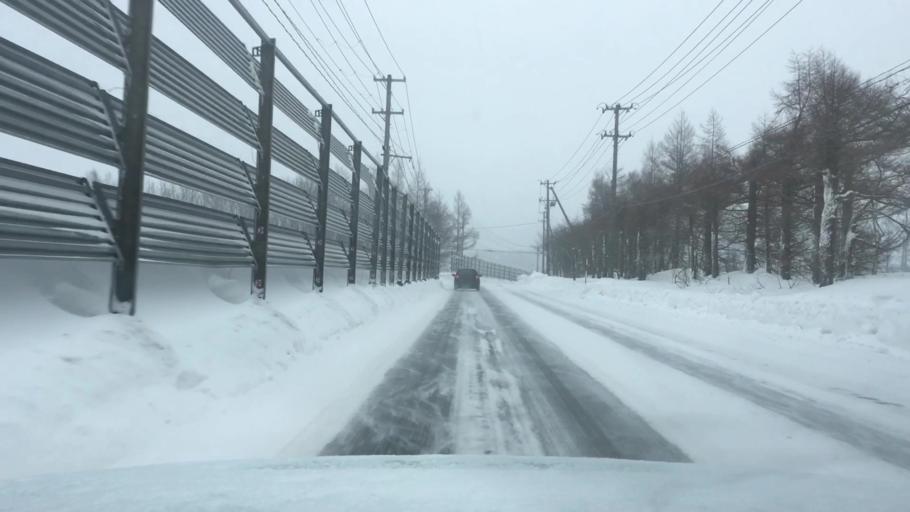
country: JP
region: Akita
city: Hanawa
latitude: 40.0110
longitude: 140.9794
